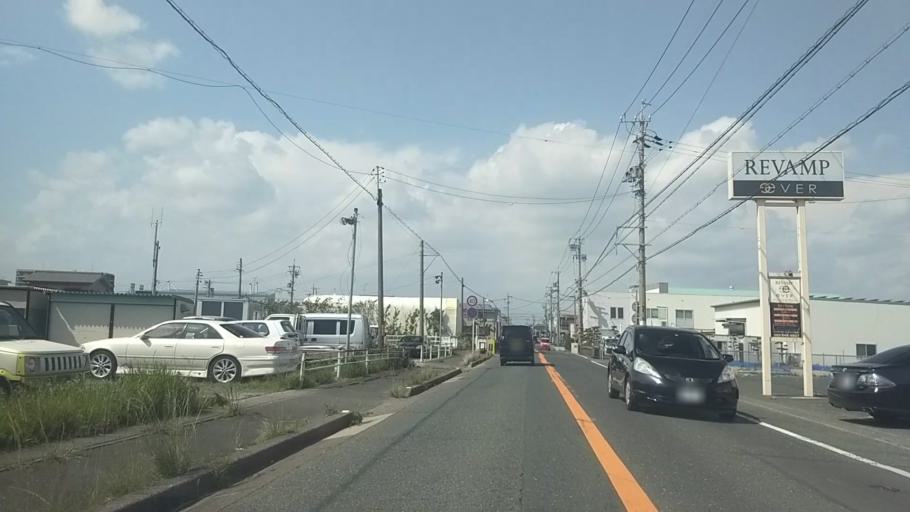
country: JP
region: Shizuoka
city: Hamamatsu
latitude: 34.6843
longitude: 137.7111
